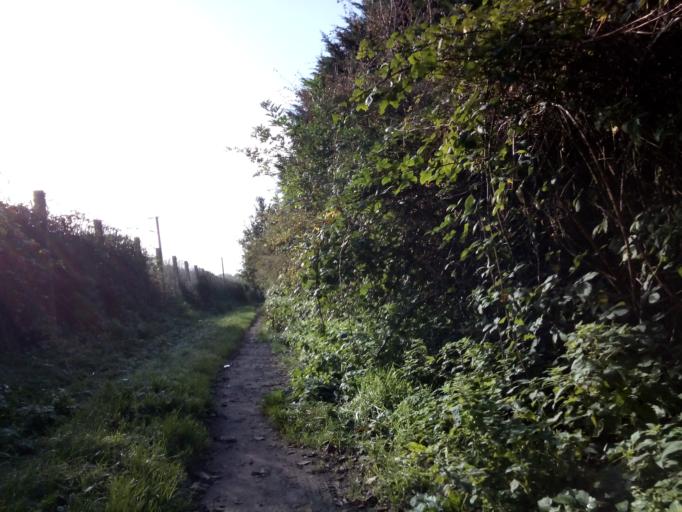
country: GB
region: England
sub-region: Suffolk
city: Ipswich
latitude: 52.0372
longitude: 1.1488
